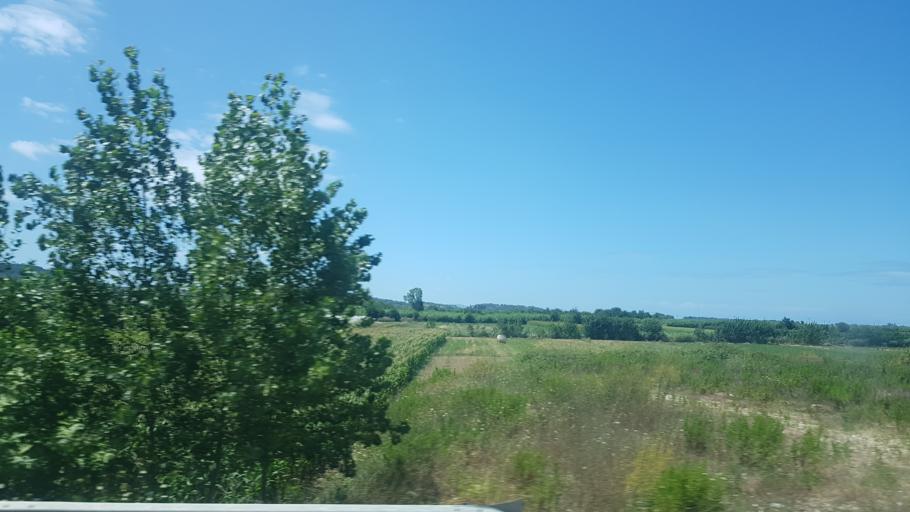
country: AL
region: Fier
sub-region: Rrethi i Fierit
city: Frakulla e Madhe
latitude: 40.6174
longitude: 19.5196
